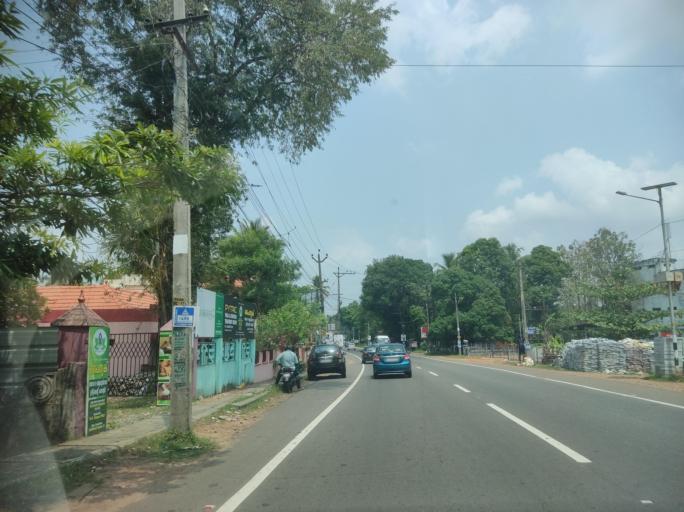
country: IN
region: Kerala
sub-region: Pattanamtitta
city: Tiruvalla
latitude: 9.4089
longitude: 76.5572
